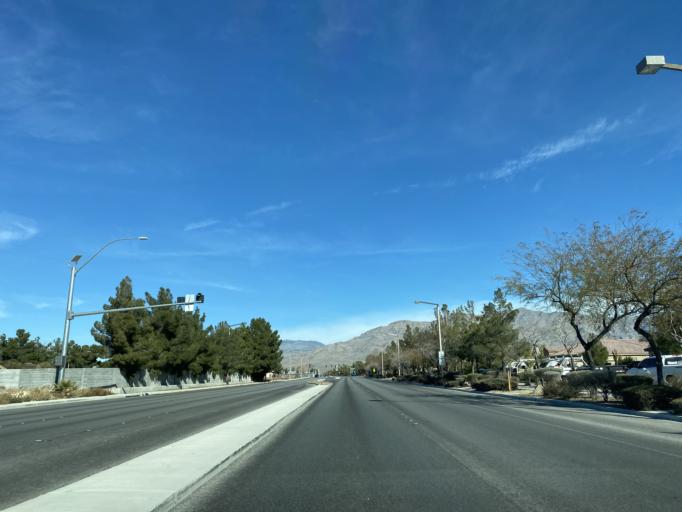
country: US
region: Nevada
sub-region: Clark County
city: North Las Vegas
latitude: 36.3018
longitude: -115.2240
